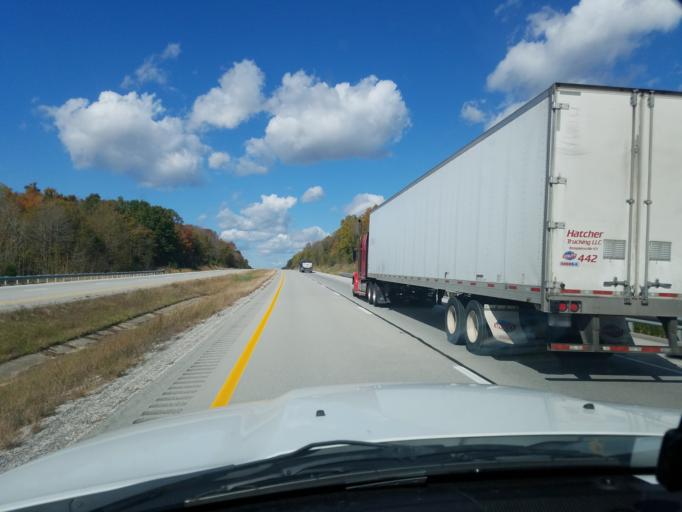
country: US
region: Kentucky
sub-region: Butler County
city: Morgantown
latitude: 37.2521
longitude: -86.7399
